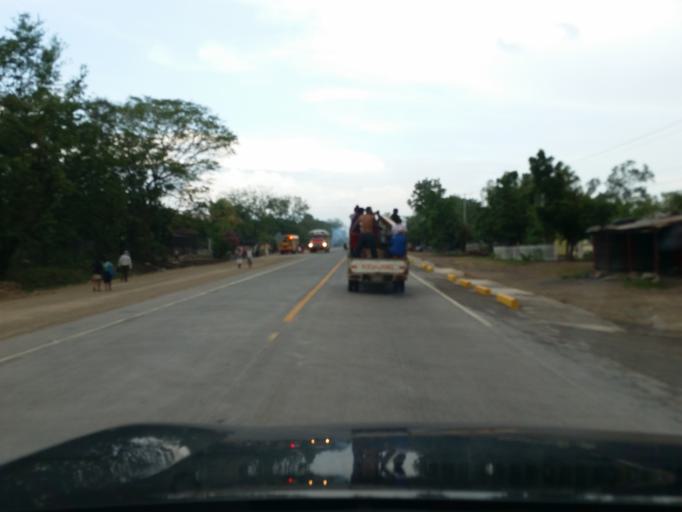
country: NI
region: Managua
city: Carlos Fonseca Amador
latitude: 12.0681
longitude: -86.4815
